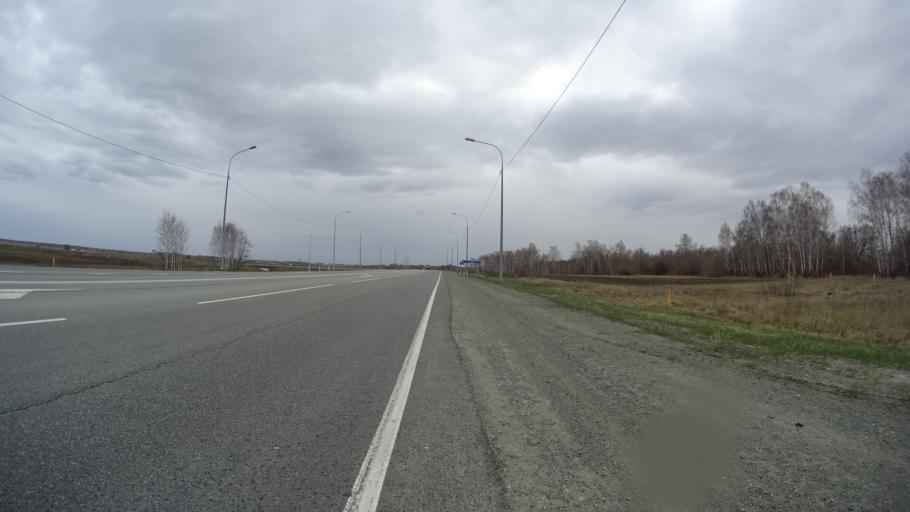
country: RU
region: Chelyabinsk
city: Krasnogorskiy
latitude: 54.6844
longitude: 61.2473
